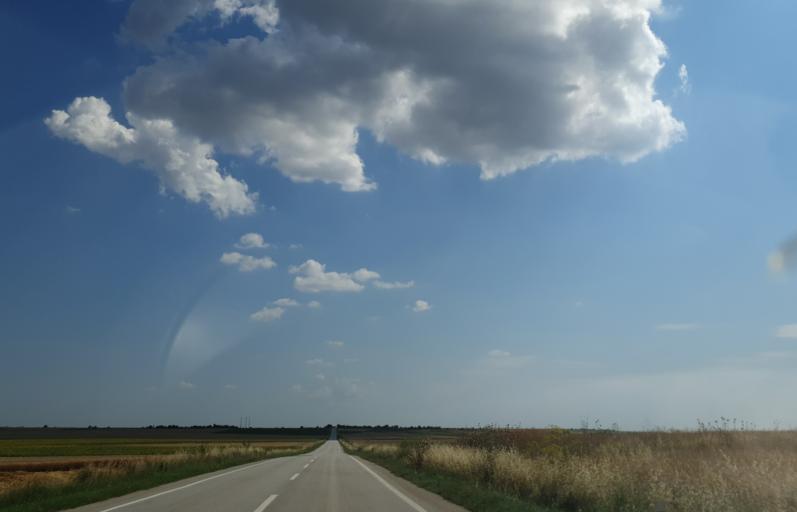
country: TR
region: Kirklareli
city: Buyukkaristiran
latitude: 41.3949
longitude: 27.5729
